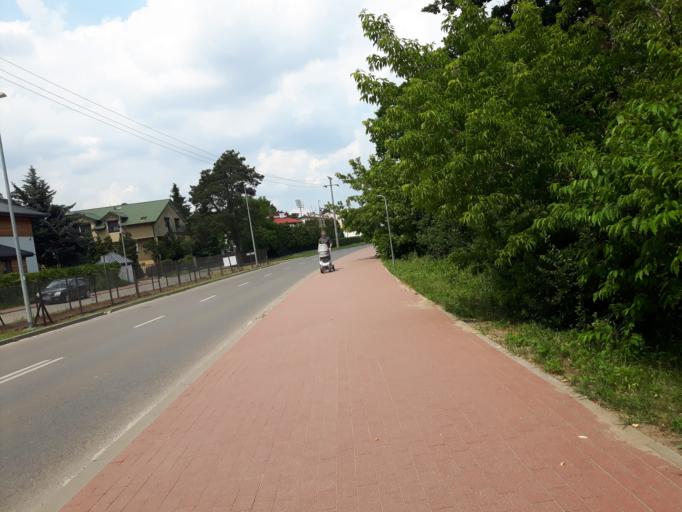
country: PL
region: Masovian Voivodeship
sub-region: Powiat wolominski
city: Zabki
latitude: 52.2883
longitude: 21.1263
